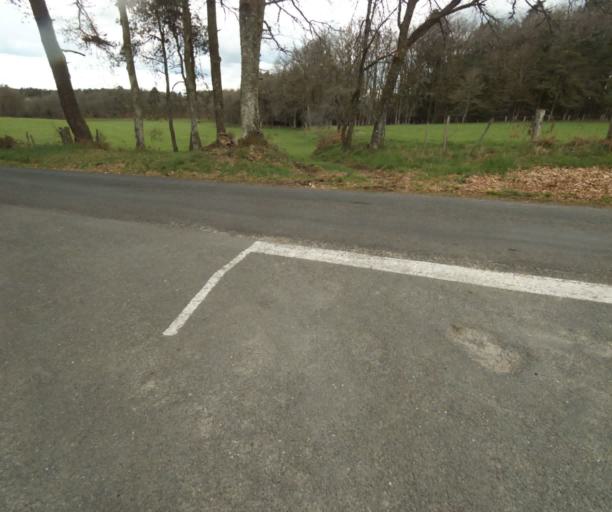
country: FR
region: Limousin
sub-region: Departement de la Correze
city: Correze
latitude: 45.3155
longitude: 1.8798
